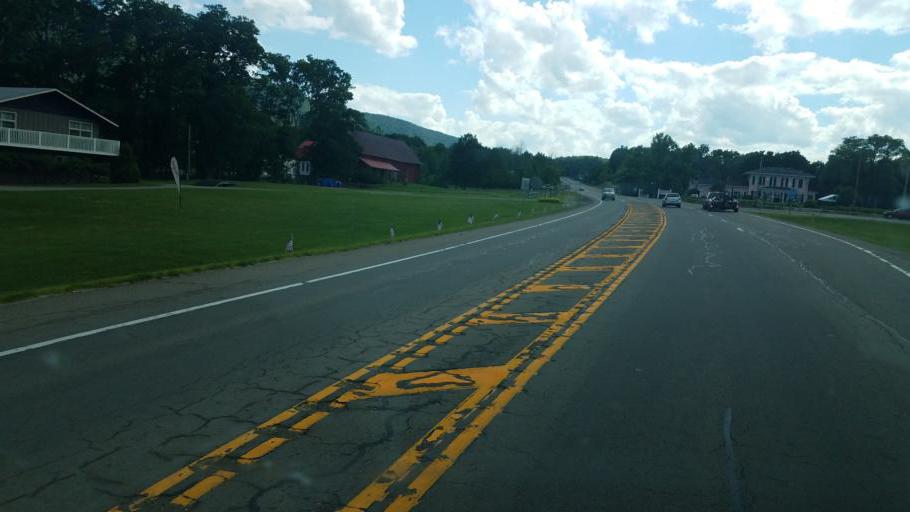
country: US
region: New York
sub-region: Steuben County
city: Bath
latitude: 42.3889
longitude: -77.2594
